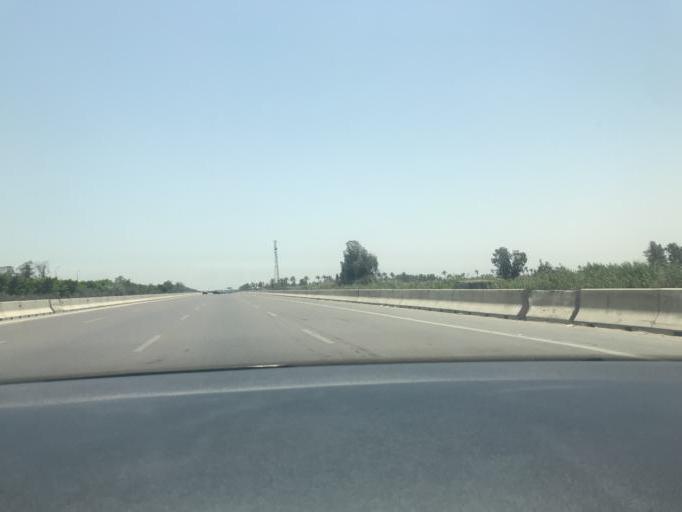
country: EG
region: Alexandria
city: Alexandria
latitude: 30.9351
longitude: 29.8501
